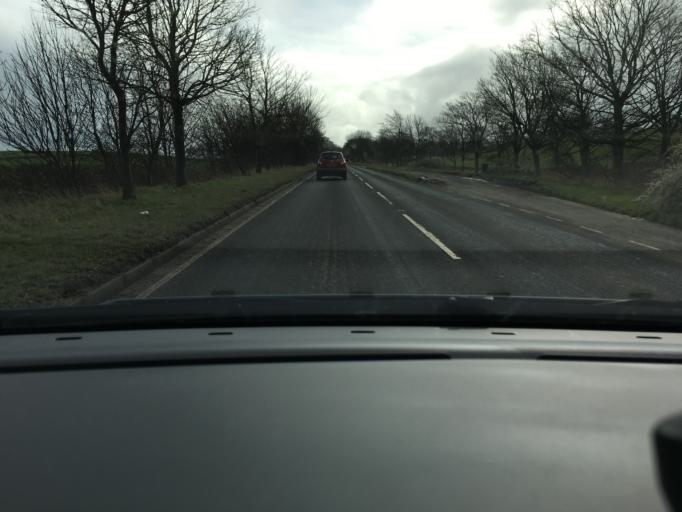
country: GB
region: Scotland
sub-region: West Lothian
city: Linlithgow
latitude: 56.0045
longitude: -3.5722
